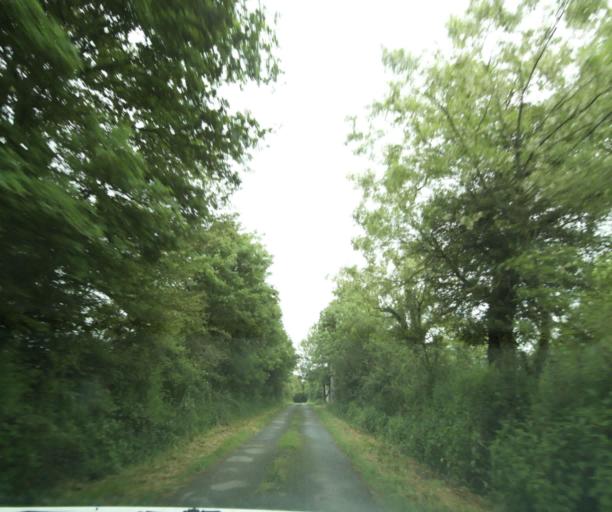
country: FR
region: Bourgogne
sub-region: Departement de Saone-et-Loire
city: Palinges
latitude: 46.5718
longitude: 4.2068
